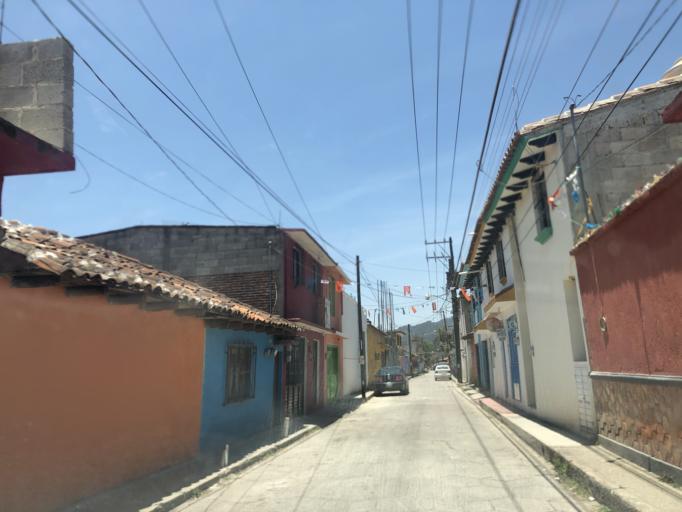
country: MX
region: Chiapas
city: San Cristobal de las Casas
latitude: 16.7312
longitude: -92.6409
